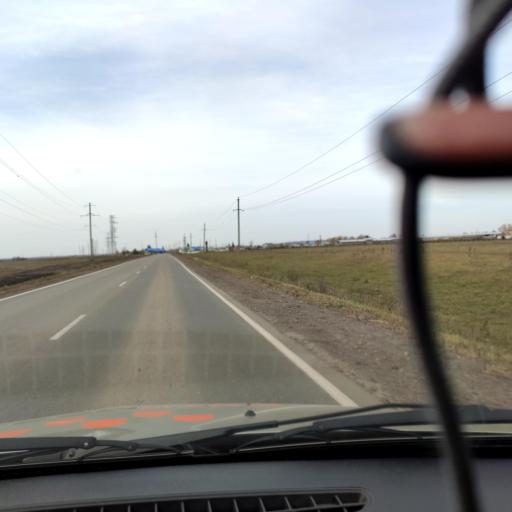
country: RU
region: Bashkortostan
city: Kabakovo
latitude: 54.5443
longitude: 56.0468
